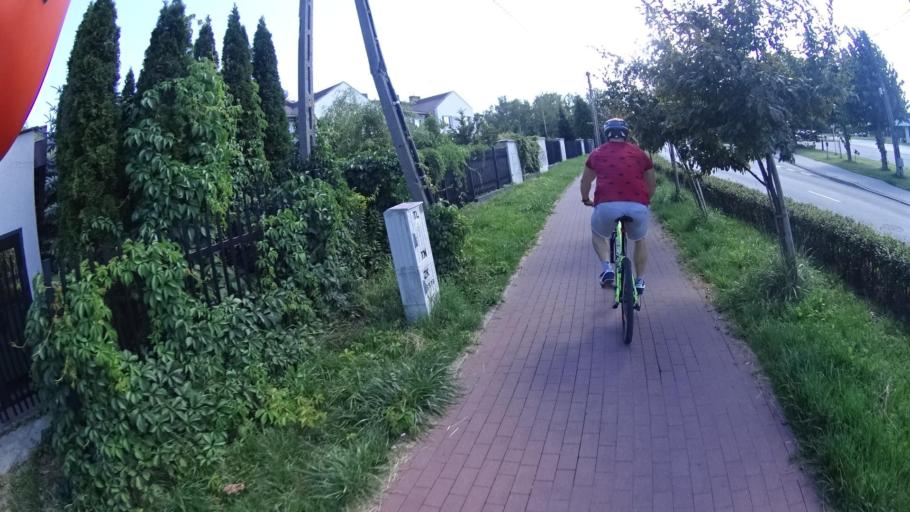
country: PL
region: Masovian Voivodeship
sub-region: Powiat piaseczynski
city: Jozefoslaw
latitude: 52.0980
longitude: 21.0535
